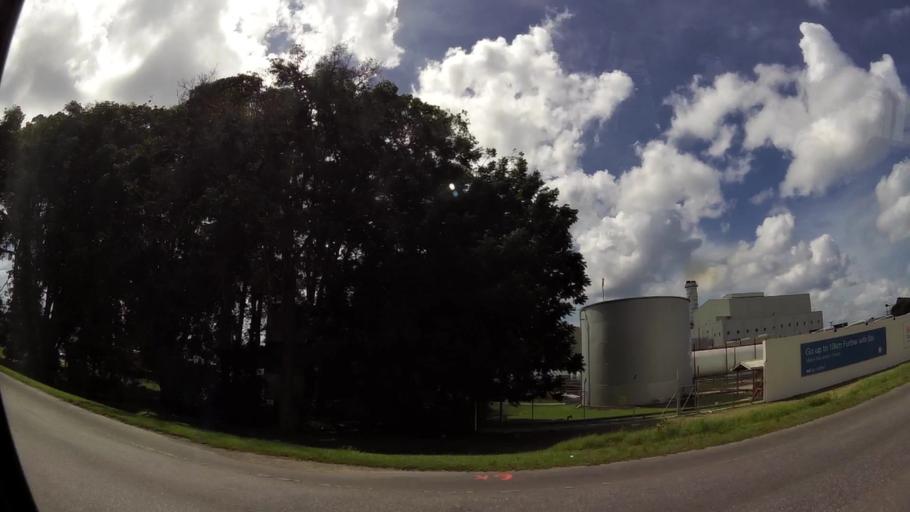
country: BB
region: Saint Michael
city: Bridgetown
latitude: 13.1264
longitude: -59.6309
